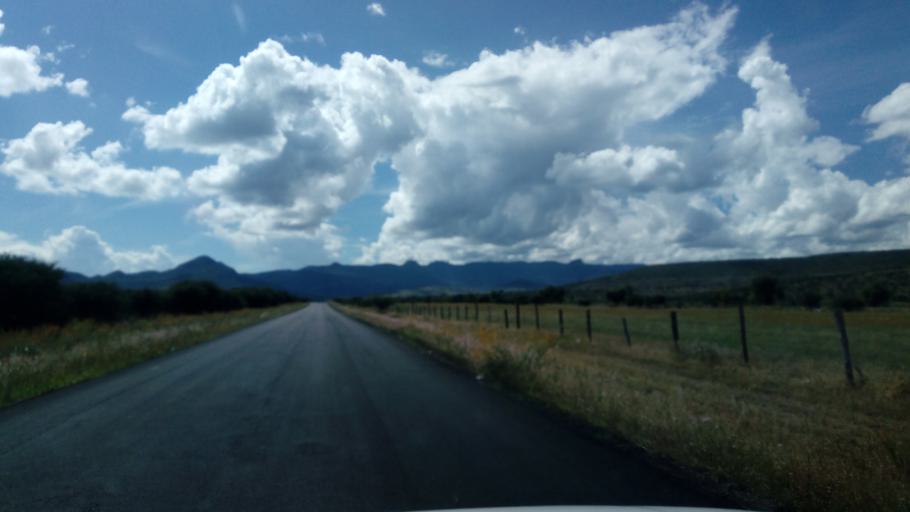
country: MX
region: Durango
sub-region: Durango
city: Jose Refugio Salcido
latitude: 23.8091
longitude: -104.4839
